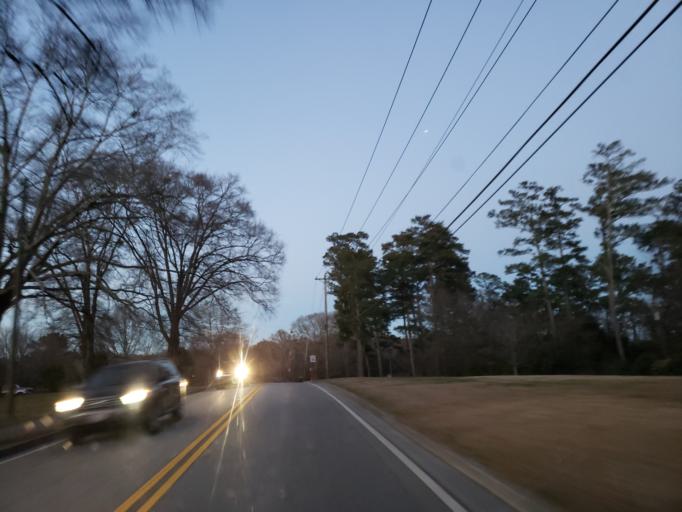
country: US
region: Georgia
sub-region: Cobb County
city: Mableton
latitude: 33.8673
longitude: -84.5676
